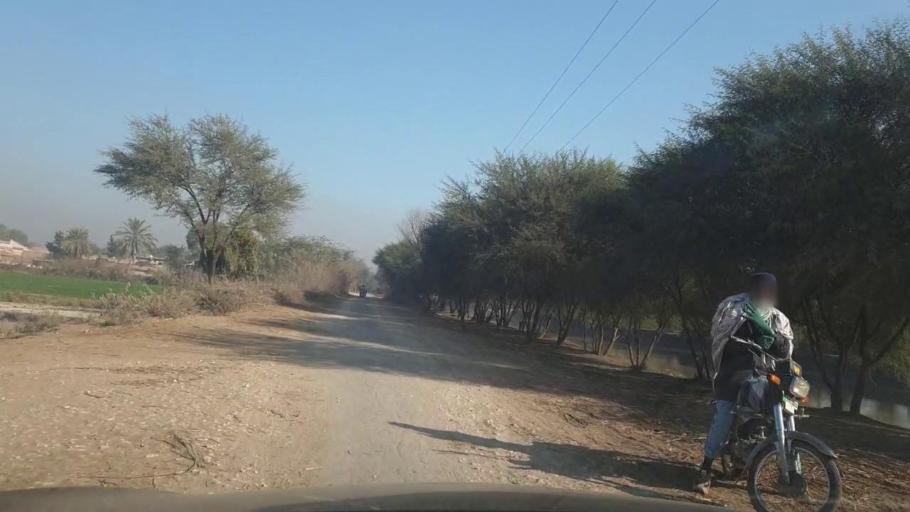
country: PK
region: Sindh
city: Mirpur Mathelo
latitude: 28.0756
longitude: 69.4684
